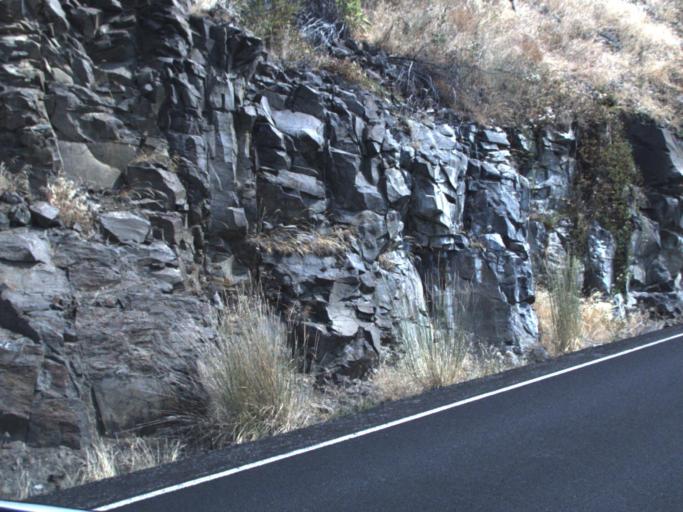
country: US
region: Washington
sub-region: Kittitas County
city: Kittitas
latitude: 46.8406
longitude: -120.4558
